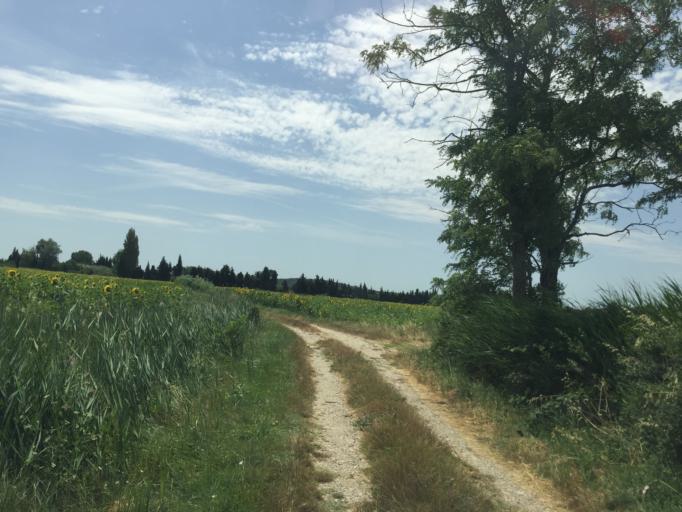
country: FR
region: Provence-Alpes-Cote d'Azur
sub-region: Departement du Vaucluse
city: Bedarrides
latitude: 44.0530
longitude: 4.8960
